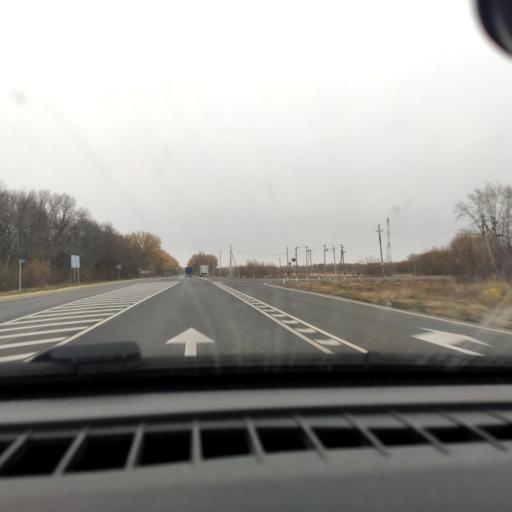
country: RU
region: Voronezj
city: Uryv-Pokrovka
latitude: 51.1699
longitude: 39.0745
